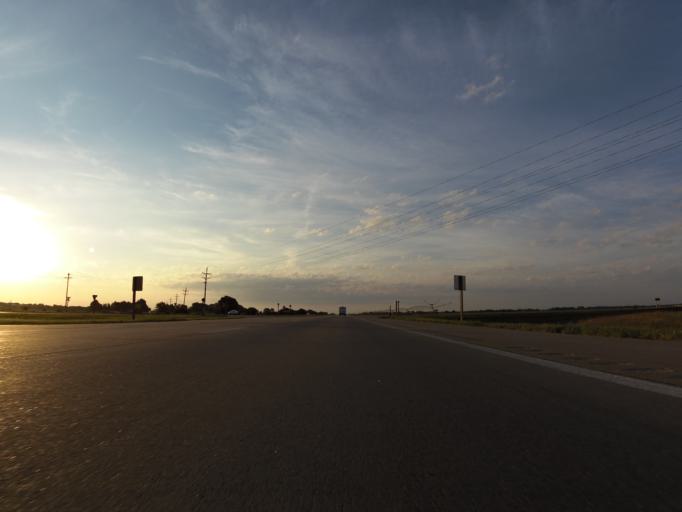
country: US
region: Kansas
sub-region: Reno County
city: South Hutchinson
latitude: 37.9557
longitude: -97.9037
